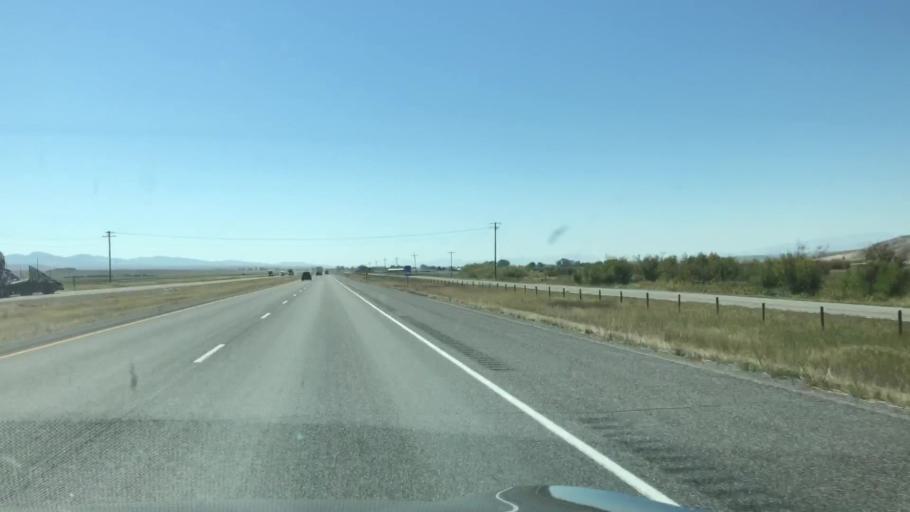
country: US
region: Montana
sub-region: Powell County
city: Deer Lodge
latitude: 46.4553
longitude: -112.7218
